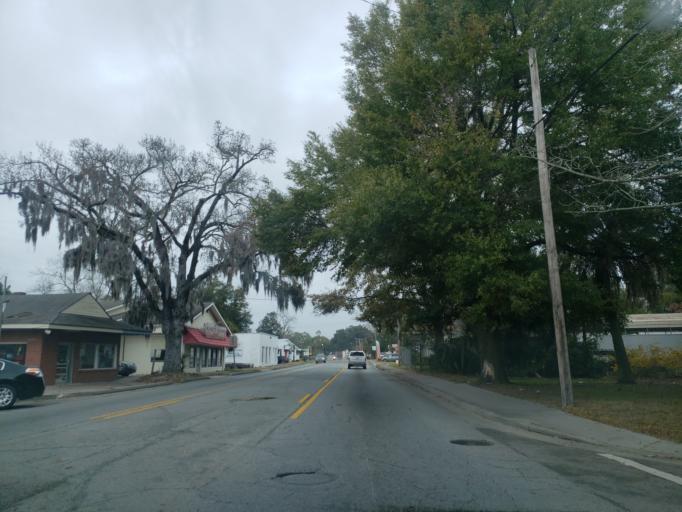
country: US
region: Georgia
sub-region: Chatham County
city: Thunderbolt
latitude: 32.0453
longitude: -81.0639
